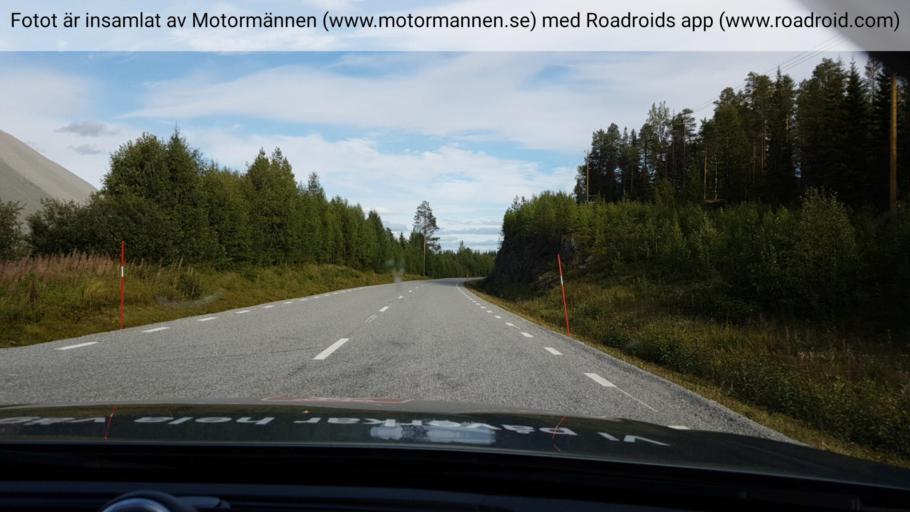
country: SE
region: Jaemtland
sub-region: Stroemsunds Kommun
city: Stroemsund
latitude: 64.1970
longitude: 15.6164
